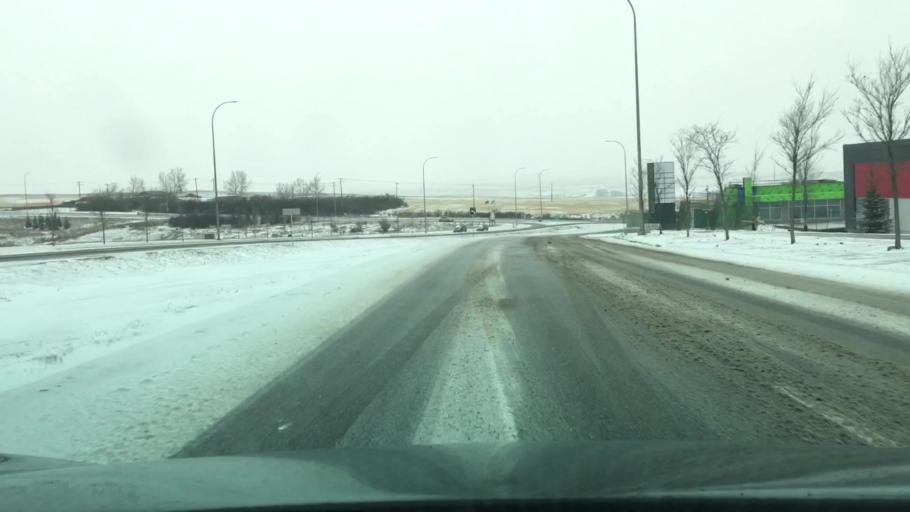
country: CA
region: Alberta
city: Calgary
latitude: 51.1807
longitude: -114.1604
